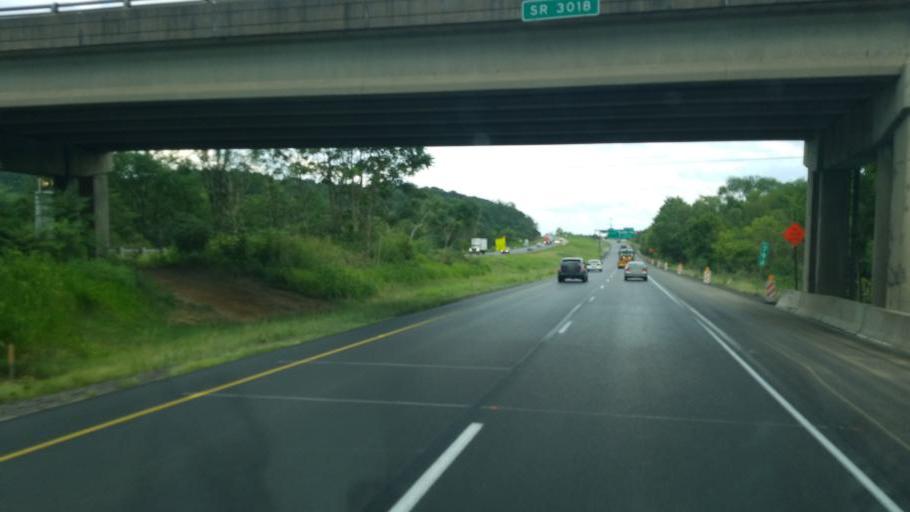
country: US
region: Pennsylvania
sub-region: Butler County
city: Fox Run
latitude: 40.7042
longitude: -80.1018
